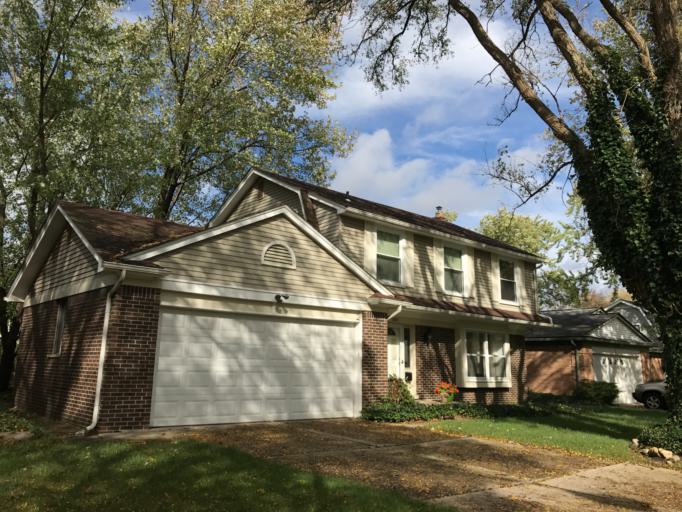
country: US
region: Michigan
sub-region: Washtenaw County
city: Ann Arbor
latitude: 42.2453
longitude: -83.7259
